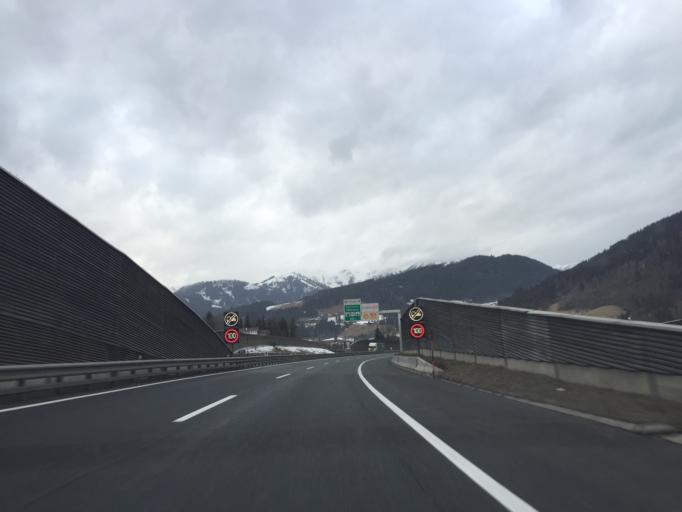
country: AT
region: Salzburg
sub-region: Politischer Bezirk Sankt Johann im Pongau
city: Eben im Pongau
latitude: 47.4115
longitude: 13.3900
